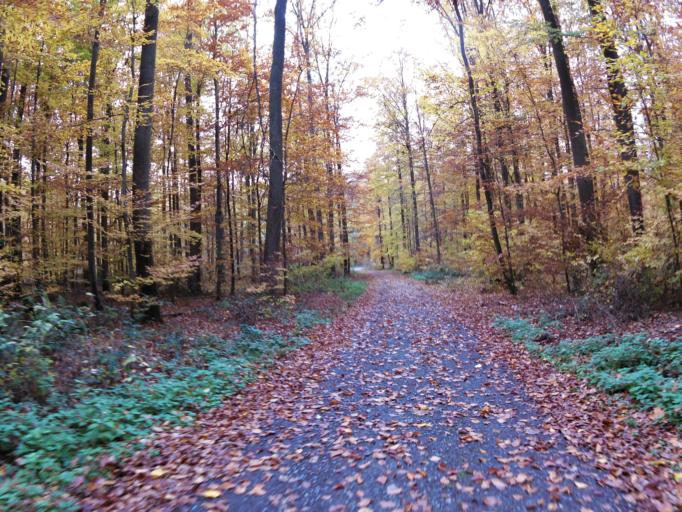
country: DE
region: Bavaria
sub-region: Regierungsbezirk Unterfranken
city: Kist
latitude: 49.7303
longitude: 9.8297
